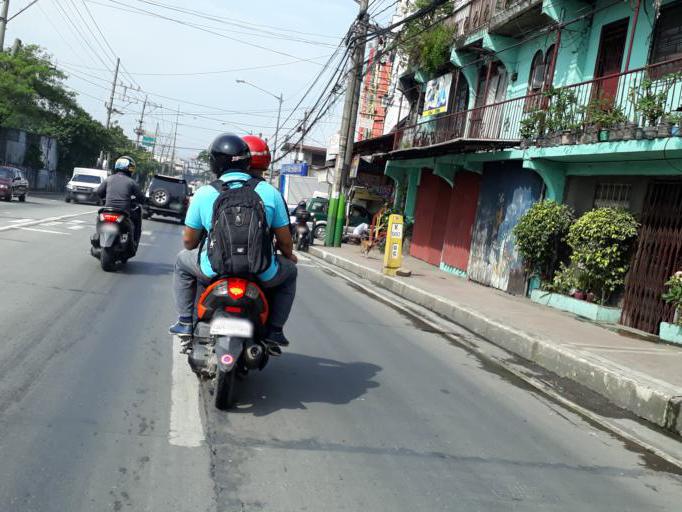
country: PH
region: Calabarzon
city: Bagong Pagasa
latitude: 14.6748
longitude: 121.0144
